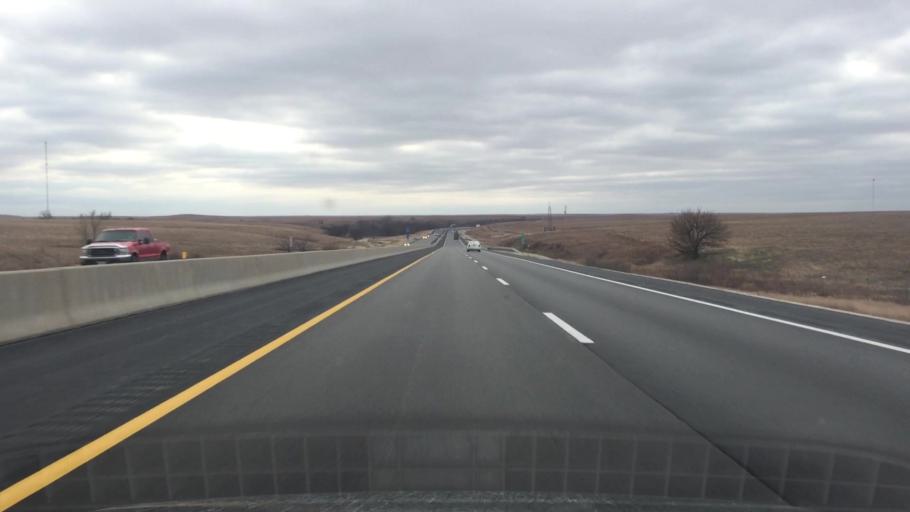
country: US
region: Kansas
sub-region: Chase County
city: Cottonwood Falls
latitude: 38.1586
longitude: -96.4869
